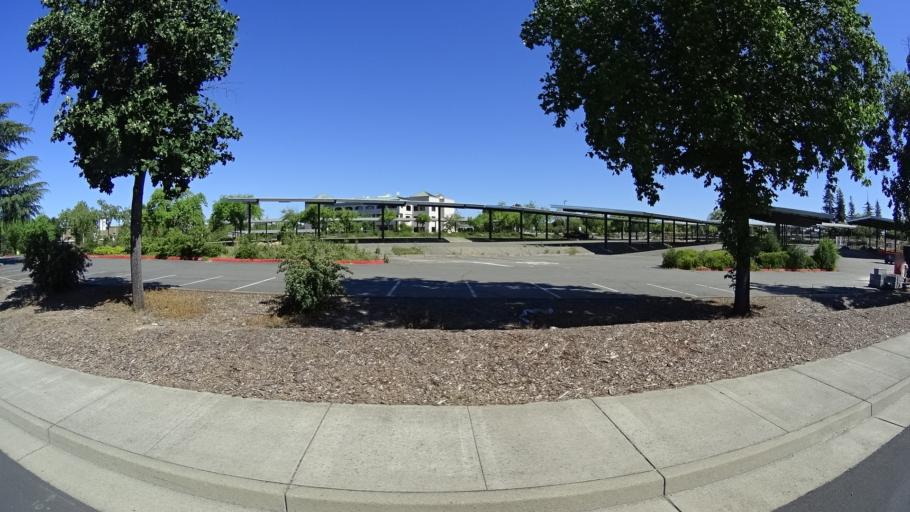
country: US
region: California
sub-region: Placer County
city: Rocklin
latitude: 38.7887
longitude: -121.2113
